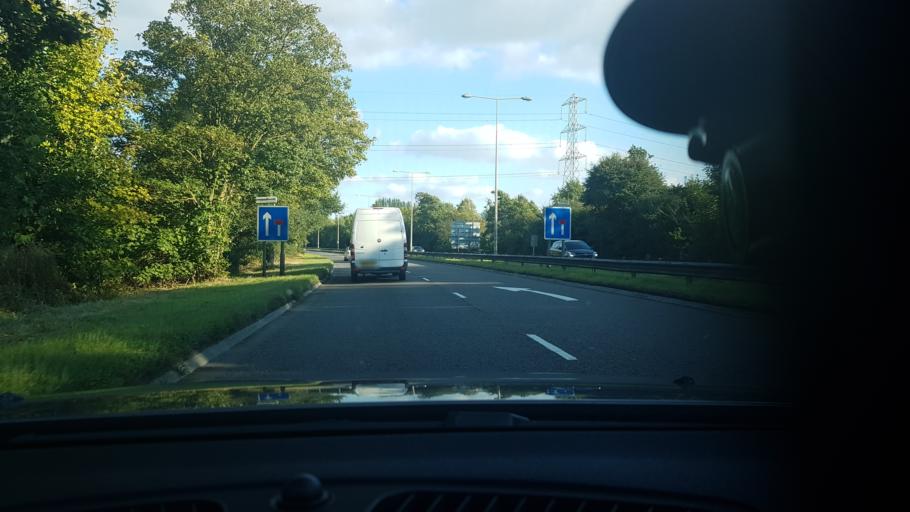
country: GB
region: England
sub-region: Gloucestershire
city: Cirencester
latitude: 51.7068
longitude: -1.9515
